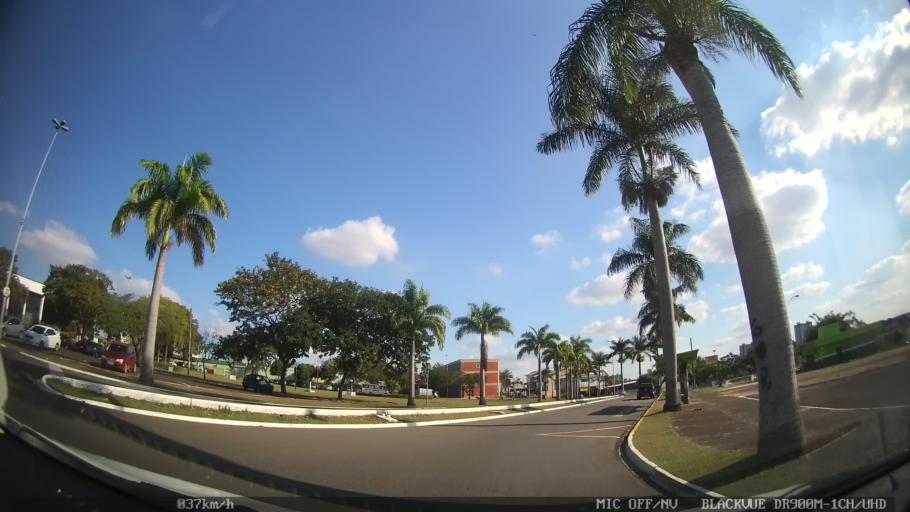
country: BR
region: Sao Paulo
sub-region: Nova Odessa
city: Nova Odessa
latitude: -22.7795
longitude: -47.2996
